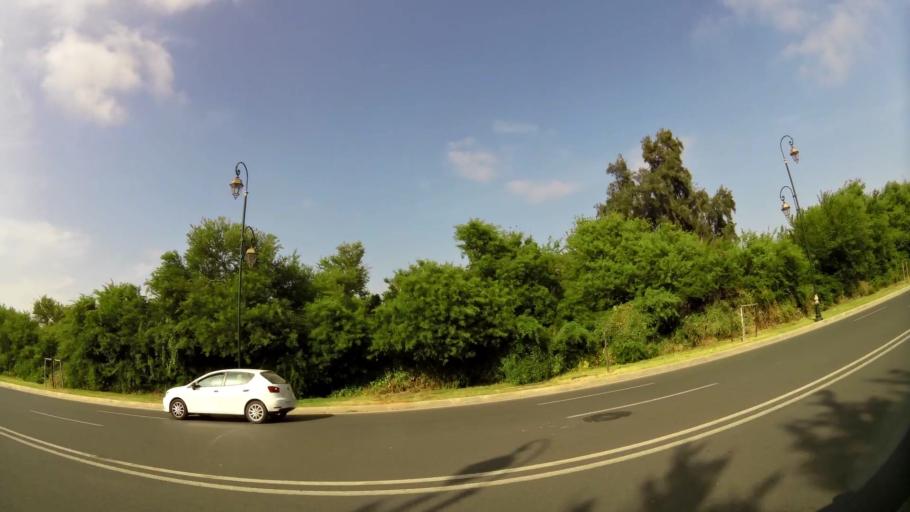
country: MA
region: Rabat-Sale-Zemmour-Zaer
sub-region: Rabat
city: Rabat
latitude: 33.9516
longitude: -6.8139
